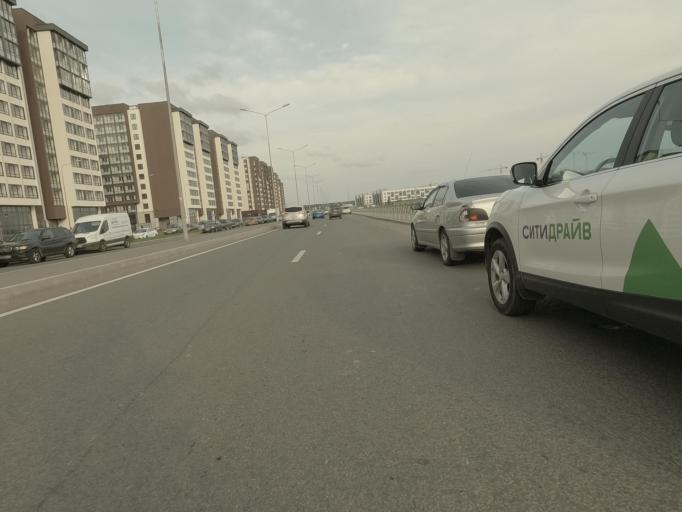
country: RU
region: St.-Petersburg
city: Sosnovaya Polyana
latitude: 59.8375
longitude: 30.1051
